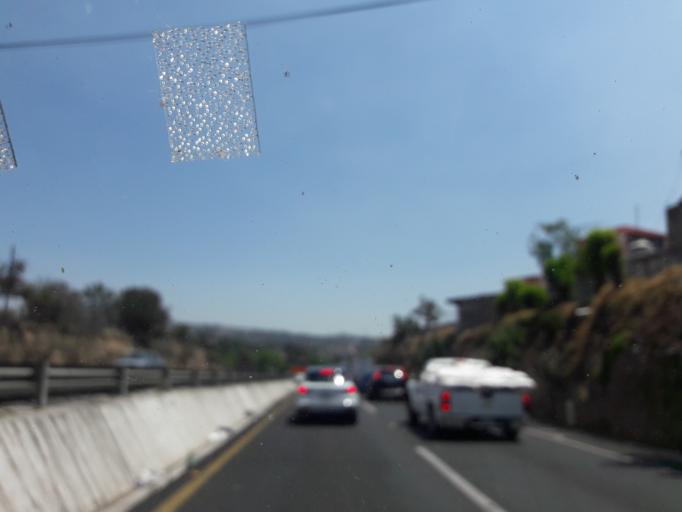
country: MX
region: Tlaxcala
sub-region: Apetatitlan de Antonio Carvajal
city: Tlatempan
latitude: 19.3405
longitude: -98.2065
